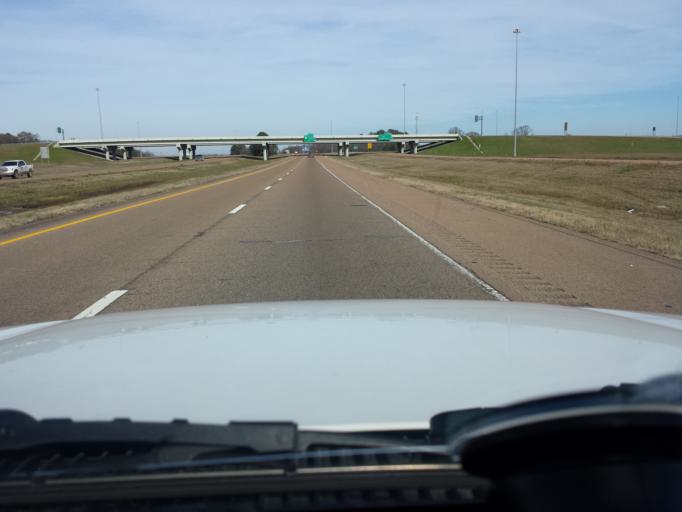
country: US
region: Mississippi
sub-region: Madison County
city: Canton
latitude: 32.5842
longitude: -90.0706
